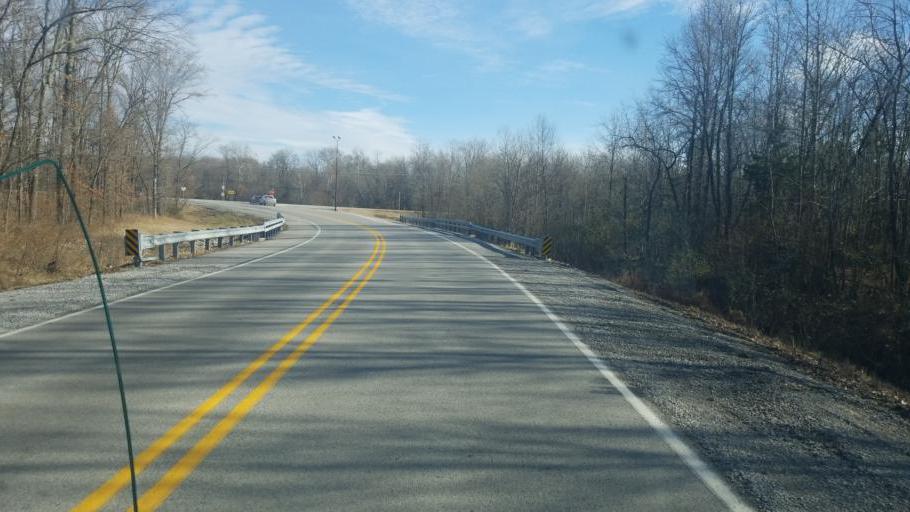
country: US
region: Illinois
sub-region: Jackson County
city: Carbondale
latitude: 37.7008
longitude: -89.1855
